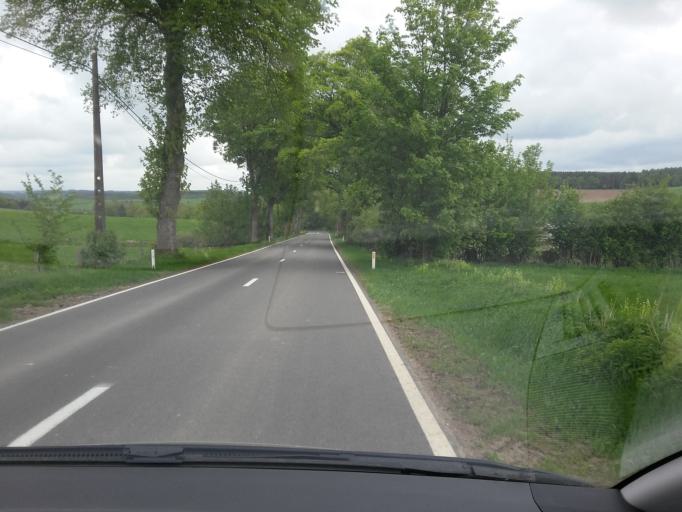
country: BE
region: Wallonia
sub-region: Province du Luxembourg
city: Neufchateau
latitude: 49.8217
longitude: 5.4176
